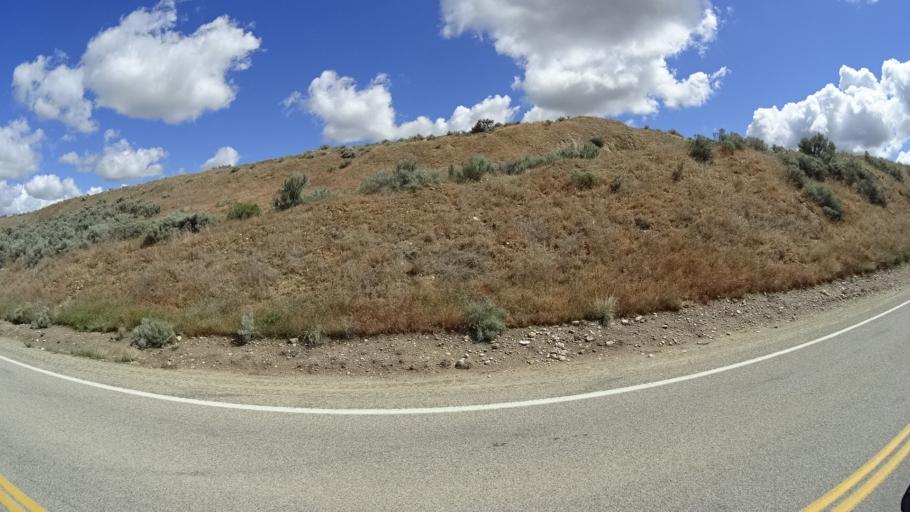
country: US
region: Idaho
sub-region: Ada County
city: Kuna
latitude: 43.5104
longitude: -116.3120
